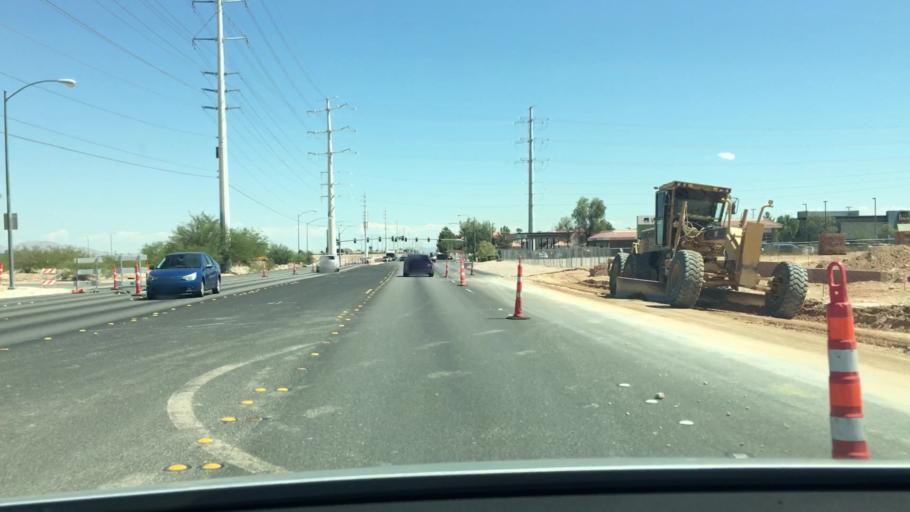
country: US
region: Nevada
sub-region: Clark County
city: Spring Valley
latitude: 36.0852
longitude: -115.2821
